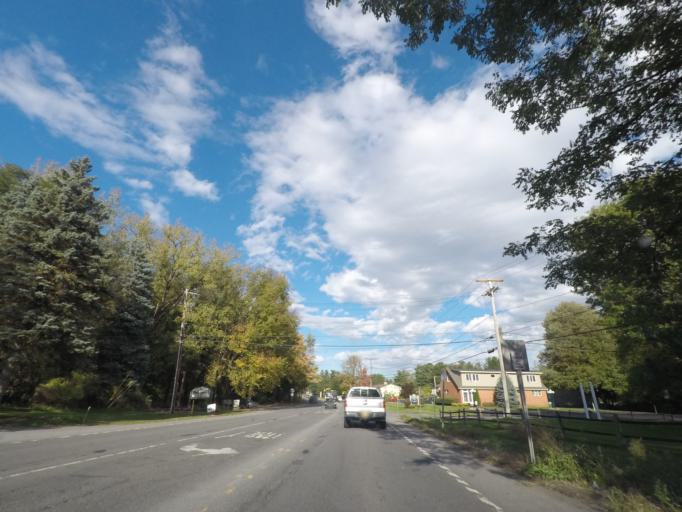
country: US
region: New York
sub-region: Schenectady County
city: Rotterdam
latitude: 42.7609
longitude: -73.9417
